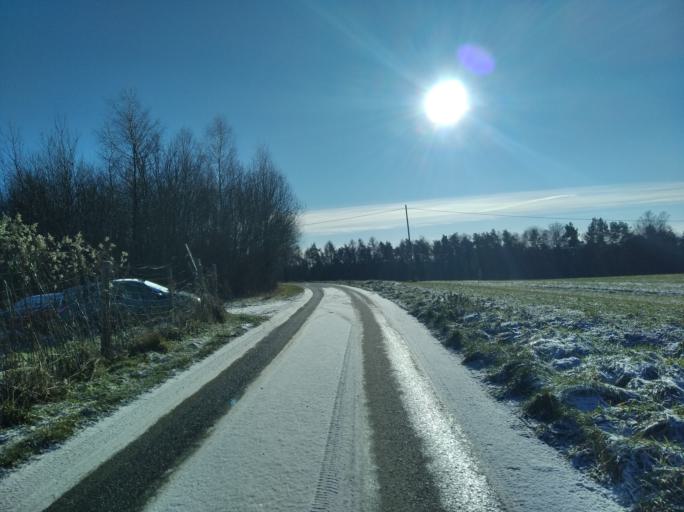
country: PL
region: Subcarpathian Voivodeship
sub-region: Powiat ropczycko-sedziszowski
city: Iwierzyce
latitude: 49.9616
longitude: 21.7512
